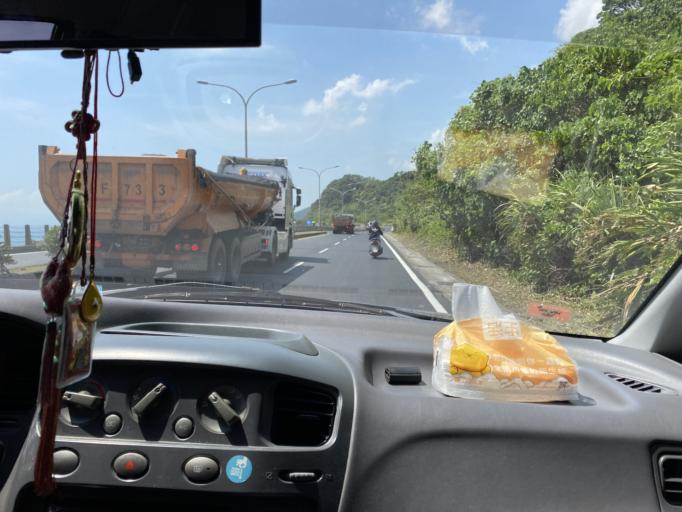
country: TW
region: Taiwan
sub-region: Yilan
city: Yilan
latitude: 24.8977
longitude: 121.8619
